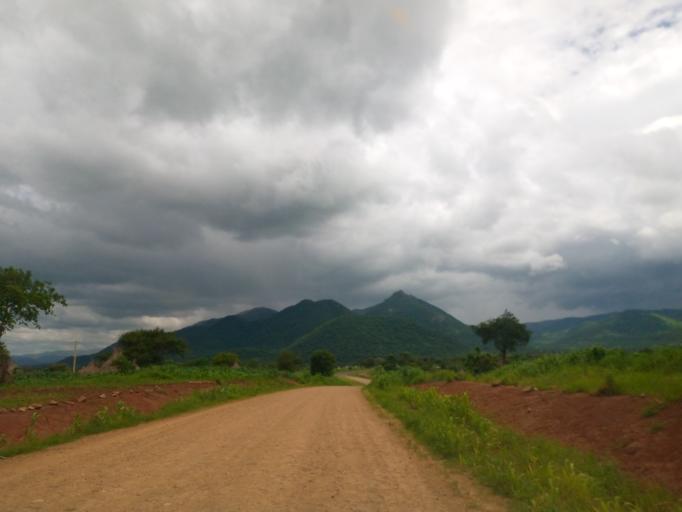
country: ET
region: Oromiya
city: Mendi
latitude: 10.1837
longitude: 35.0930
